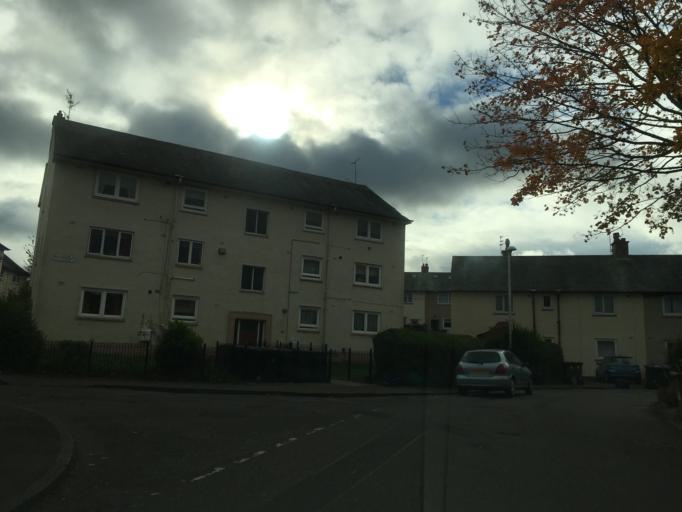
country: GB
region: Scotland
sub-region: Midlothian
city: Loanhead
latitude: 55.9183
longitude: -3.1603
